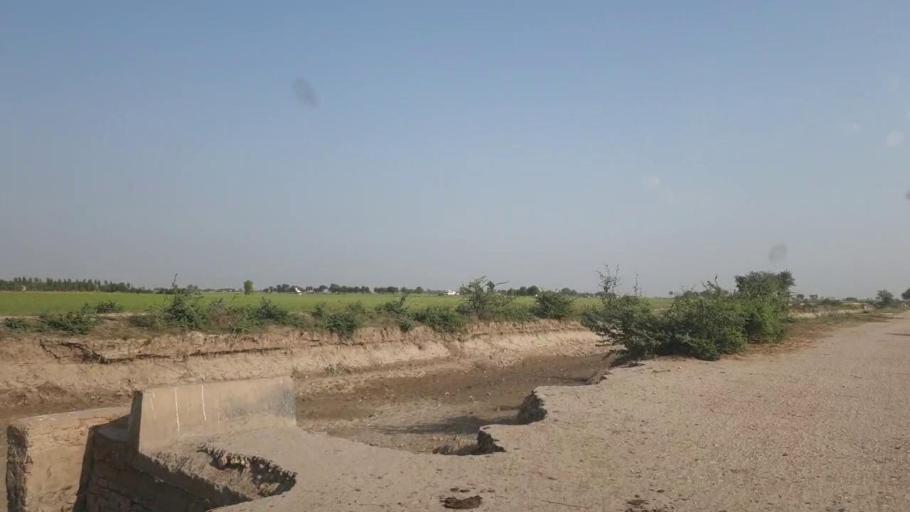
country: PK
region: Sindh
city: Kario
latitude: 24.6000
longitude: 68.5518
